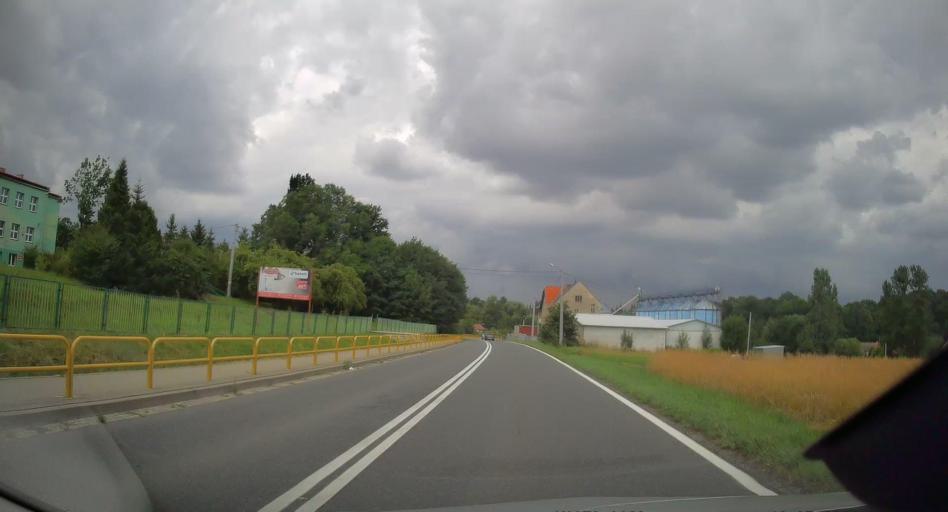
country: PL
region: Opole Voivodeship
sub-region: Powiat prudnicki
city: Laka Prudnicka
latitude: 50.3805
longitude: 17.5286
